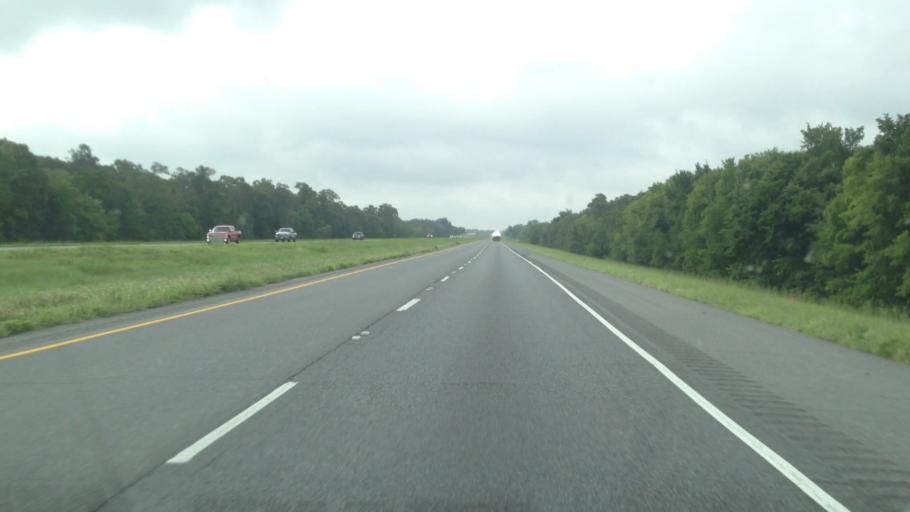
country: US
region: Louisiana
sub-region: Saint Landry Parish
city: Opelousas
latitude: 30.6628
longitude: -92.0679
